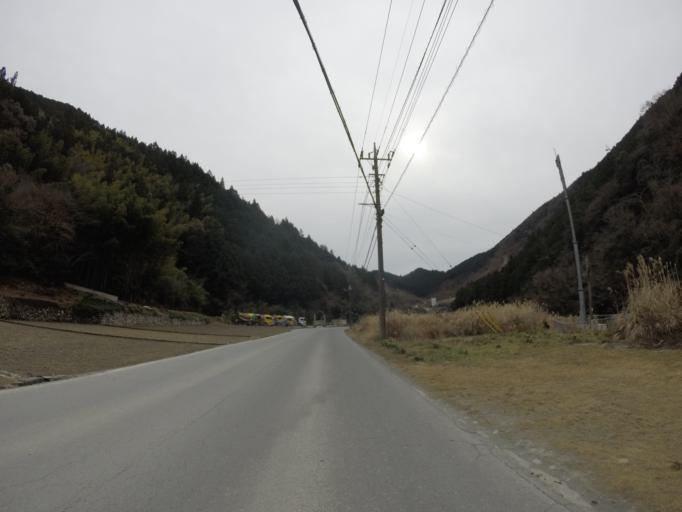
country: JP
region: Shizuoka
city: Fujinomiya
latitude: 35.2423
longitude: 138.5288
